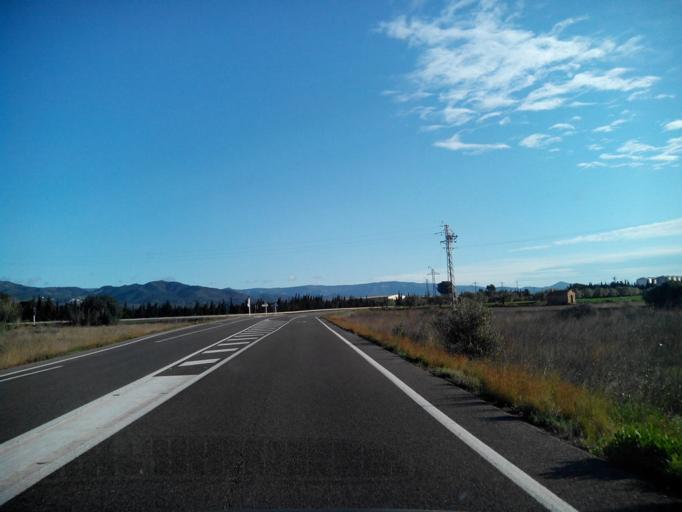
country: ES
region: Catalonia
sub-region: Provincia de Tarragona
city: Riudecanyes
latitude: 41.0950
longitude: 0.9730
